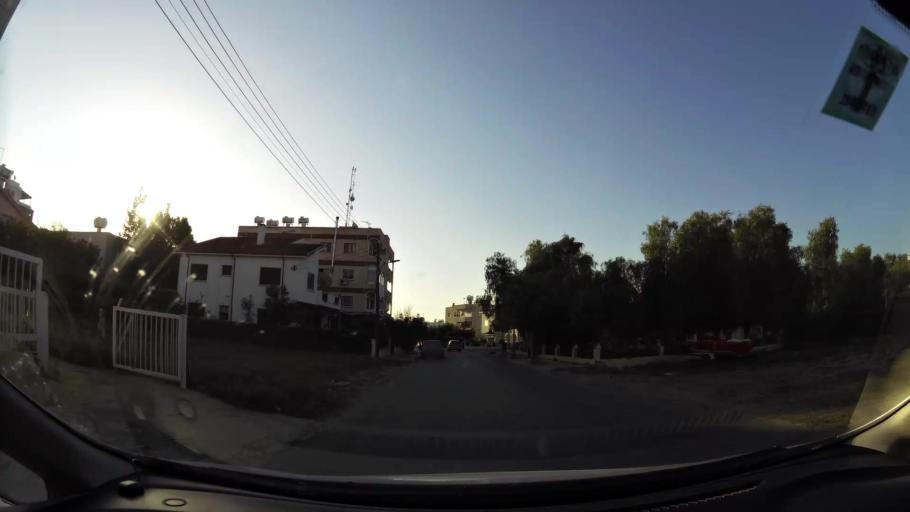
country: CY
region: Lefkosia
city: Nicosia
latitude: 35.2058
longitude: 33.3160
